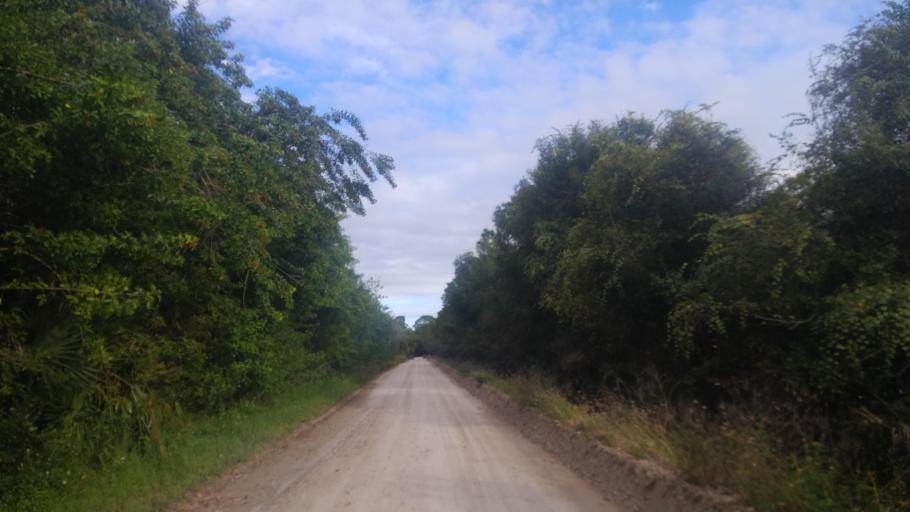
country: US
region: Florida
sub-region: Indian River County
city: Fellsmere
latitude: 27.7609
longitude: -80.5804
